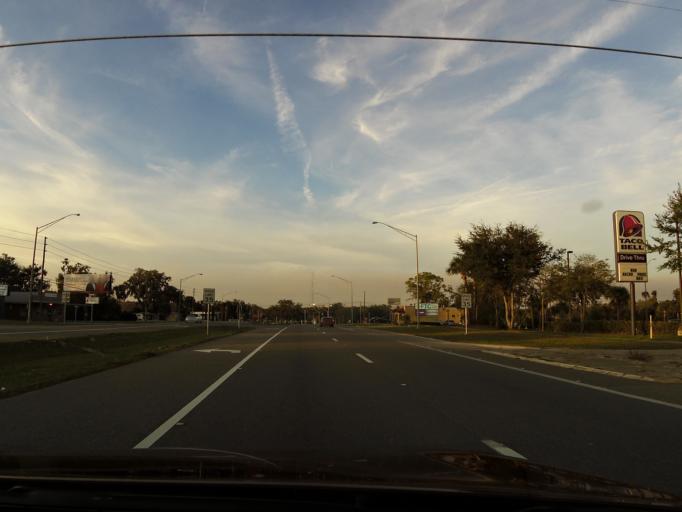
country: US
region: Florida
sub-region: Volusia County
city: De Land Southwest
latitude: 29.0083
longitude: -81.3027
